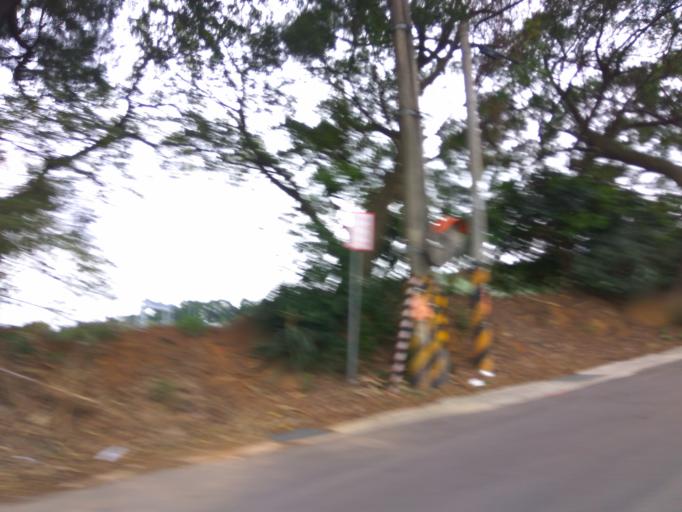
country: TW
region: Taiwan
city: Taoyuan City
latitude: 24.9817
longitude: 121.2281
